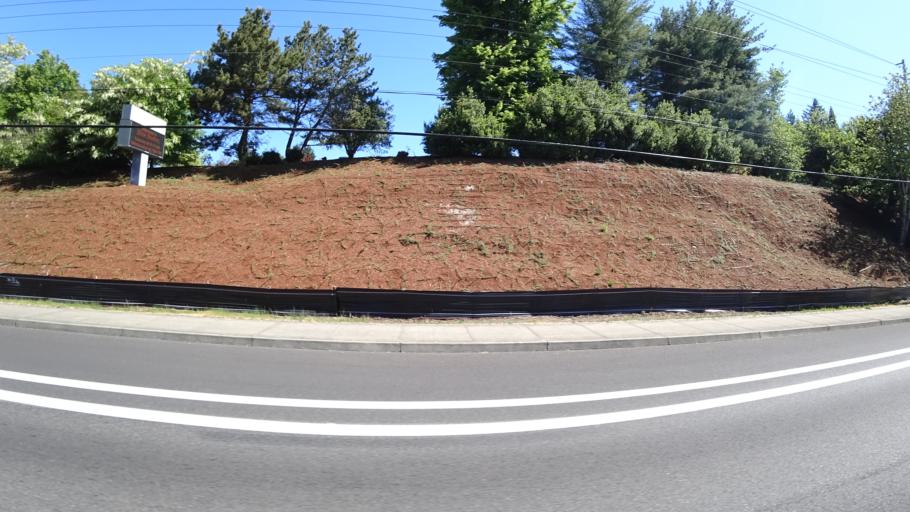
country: US
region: Oregon
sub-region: Multnomah County
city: Portland
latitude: 45.4817
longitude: -122.7060
